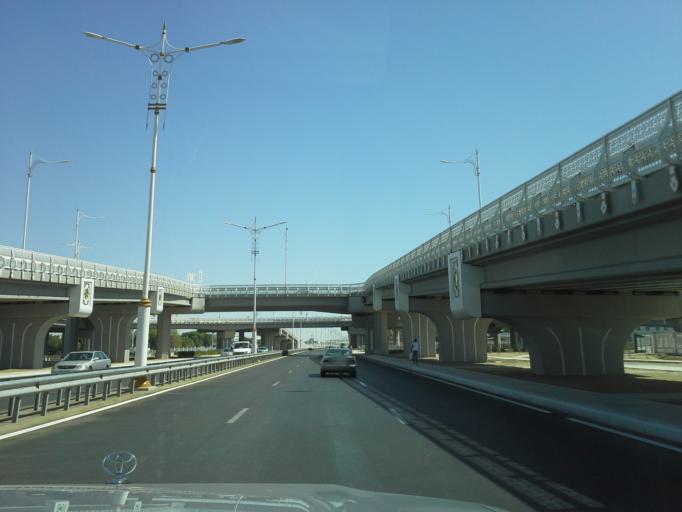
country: TM
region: Ahal
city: Ashgabat
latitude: 37.9410
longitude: 58.3992
